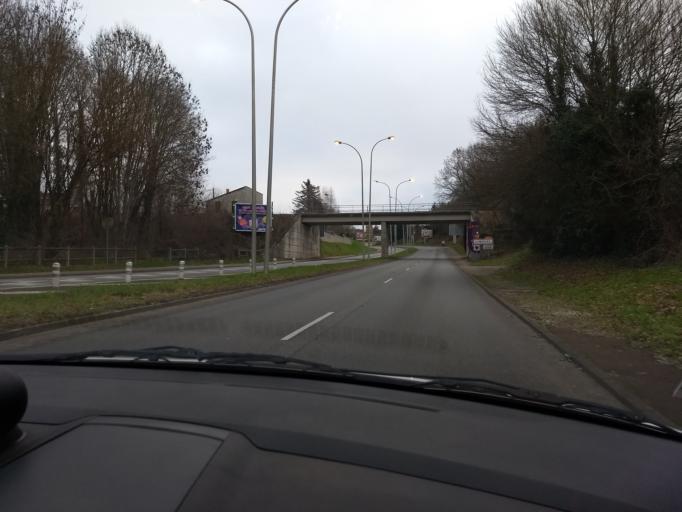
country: FR
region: Limousin
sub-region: Departement de la Haute-Vienne
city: Isle
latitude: 45.8215
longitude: 1.2131
